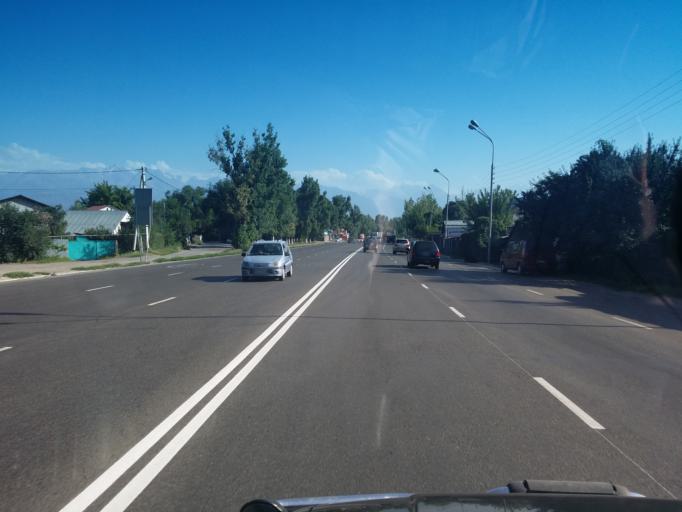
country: KZ
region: Almaty Oblysy
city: Pervomayskiy
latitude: 43.3428
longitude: 76.9326
